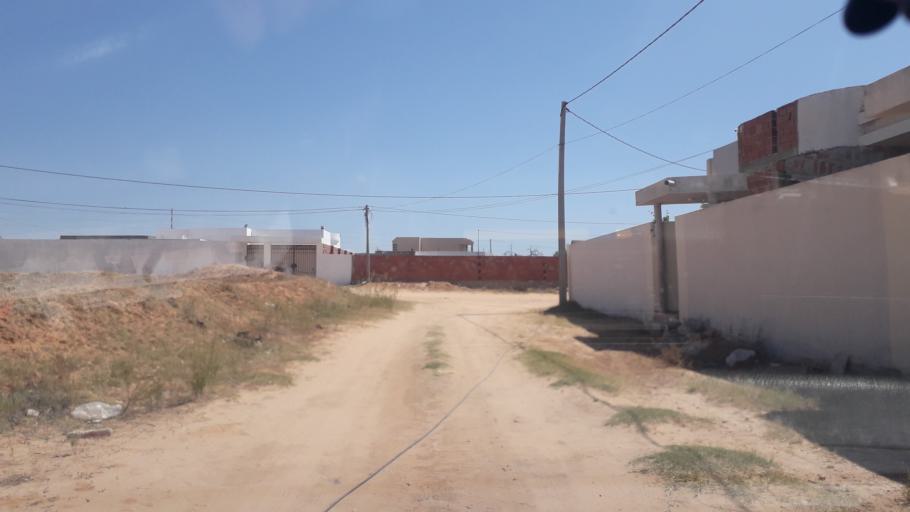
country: TN
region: Safaqis
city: Al Qarmadah
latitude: 34.8314
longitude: 10.7708
